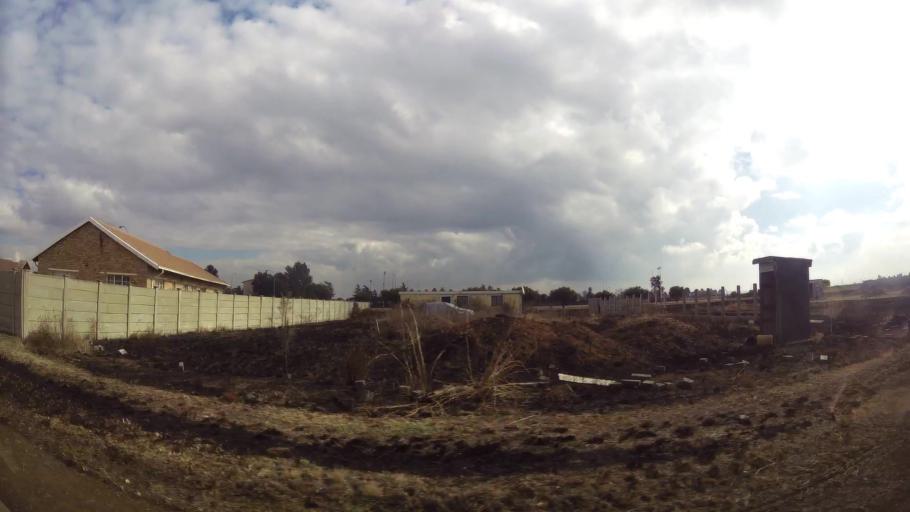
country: ZA
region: Gauteng
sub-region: Sedibeng District Municipality
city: Meyerton
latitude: -26.6021
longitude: 28.0490
